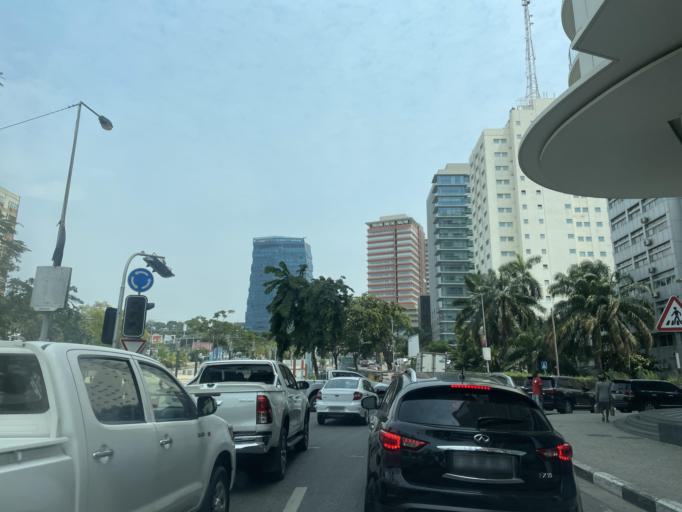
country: AO
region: Luanda
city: Luanda
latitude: -8.8083
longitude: 13.2392
